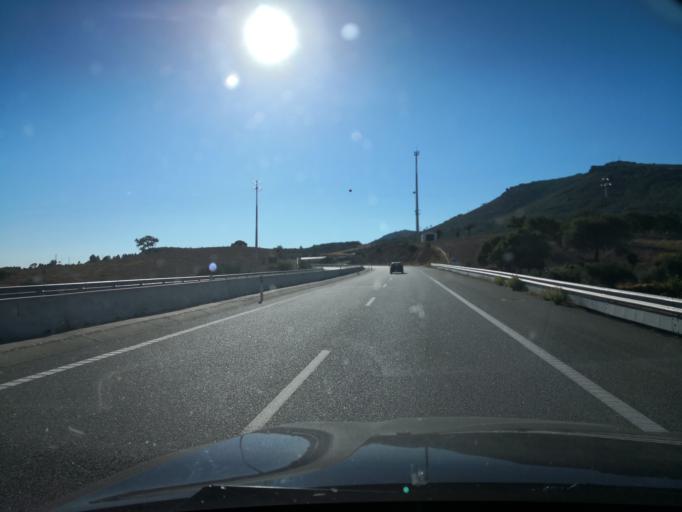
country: PT
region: Braganca
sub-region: Mirandela
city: Mirandela
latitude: 41.4613
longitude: -7.2586
